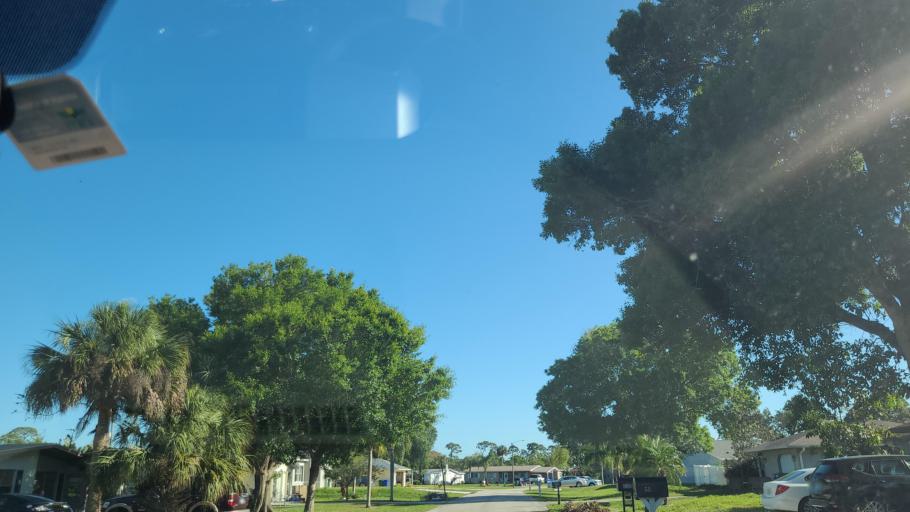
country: US
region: Florida
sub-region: Indian River County
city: Sebastian
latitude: 27.7986
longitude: -80.4855
